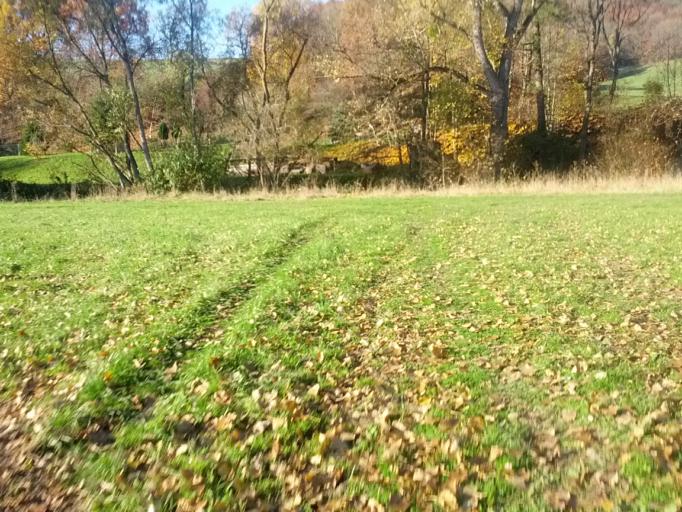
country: DE
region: Thuringia
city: Seebach
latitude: 50.9455
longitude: 10.4664
